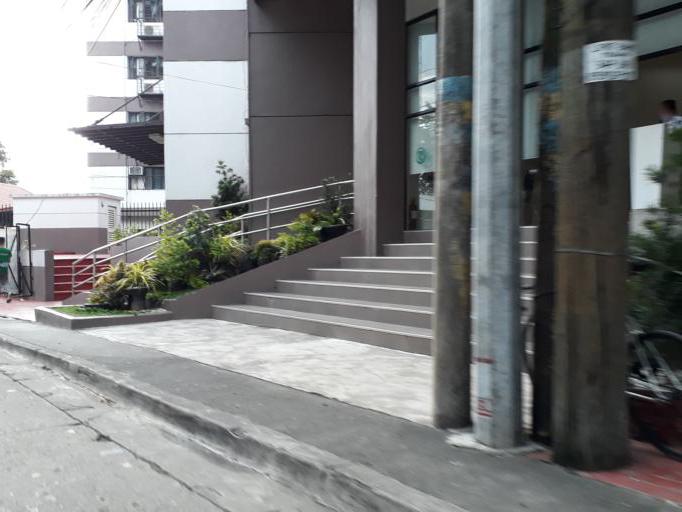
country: PH
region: Calabarzon
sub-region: Province of Rizal
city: Valenzuela
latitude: 14.6809
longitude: 120.9805
